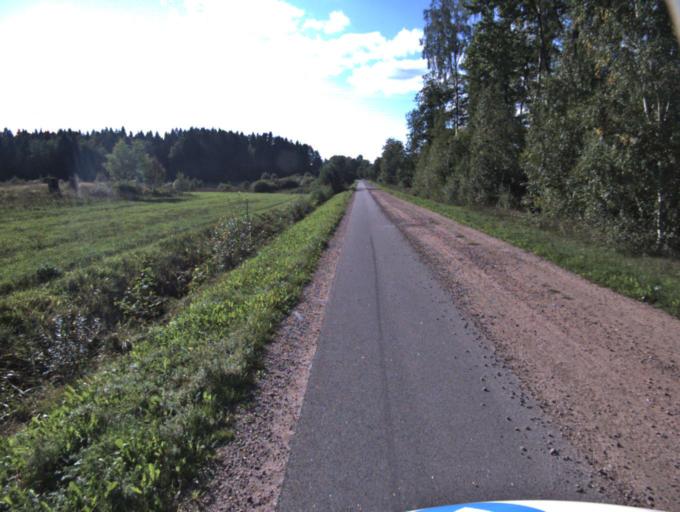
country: SE
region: Vaestra Goetaland
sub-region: Boras Kommun
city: Dalsjofors
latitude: 57.8250
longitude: 13.1681
